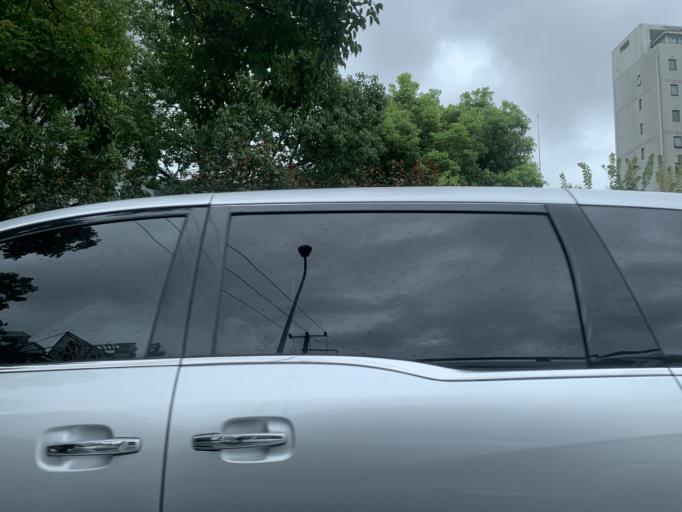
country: CN
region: Shanghai Shi
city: Huamu
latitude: 31.2017
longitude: 121.5292
